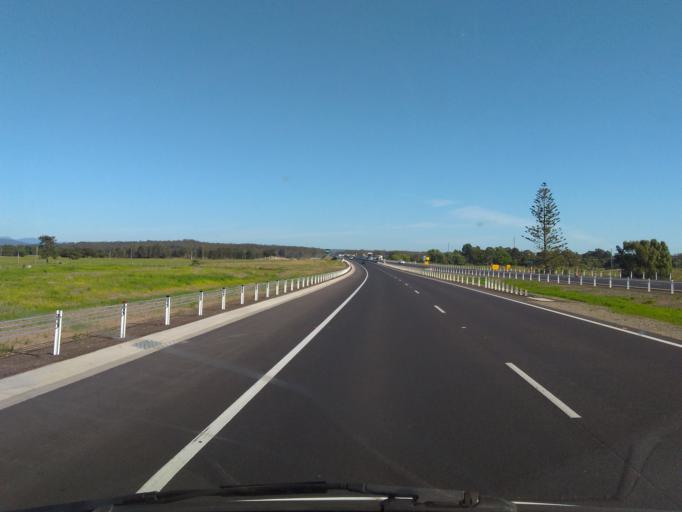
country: AU
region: New South Wales
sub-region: Port Macquarie-Hastings
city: North Shore
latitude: -31.4182
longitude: 152.8228
